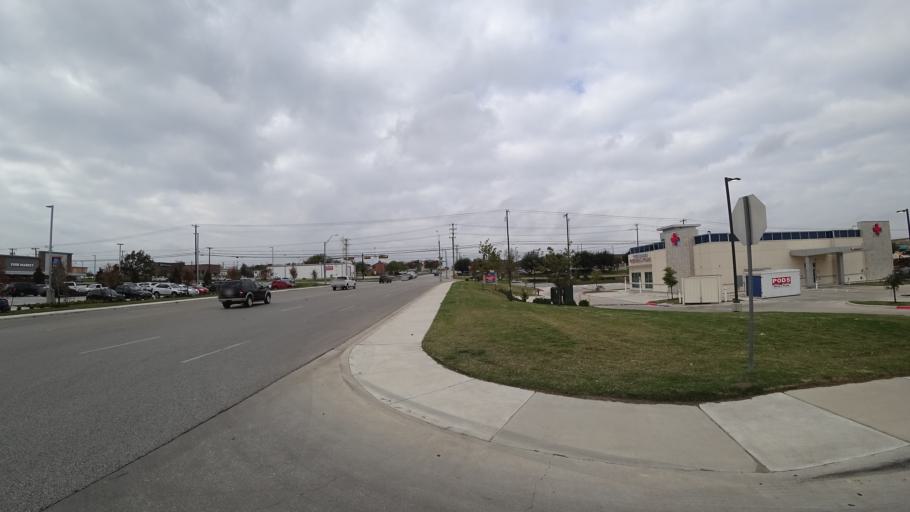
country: US
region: Texas
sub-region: Travis County
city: Pflugerville
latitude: 30.4505
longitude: -97.6040
